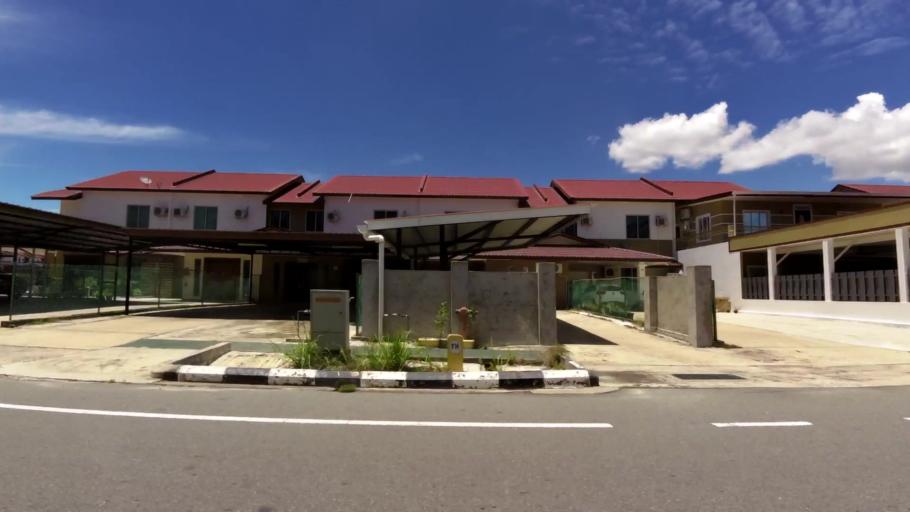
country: BN
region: Brunei and Muara
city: Bandar Seri Begawan
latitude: 5.0125
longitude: 115.0075
